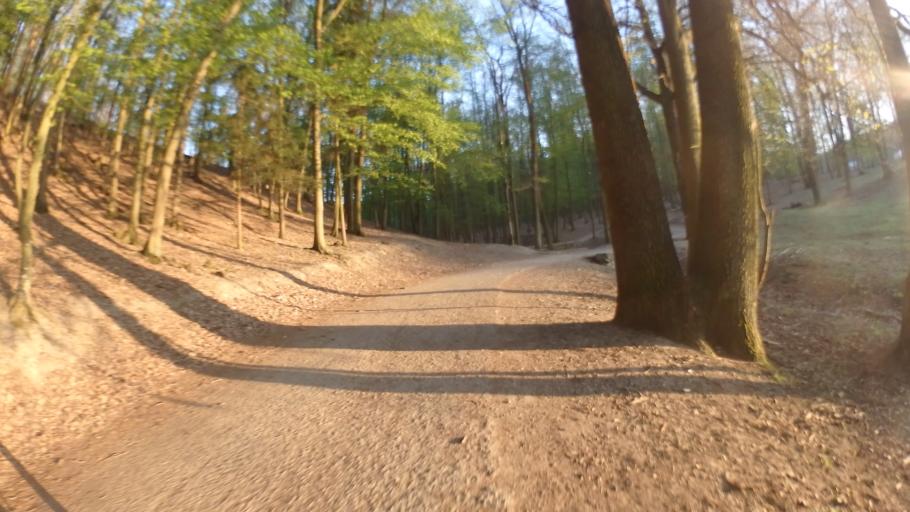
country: CZ
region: South Moravian
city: Troubsko
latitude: 49.2024
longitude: 16.5199
